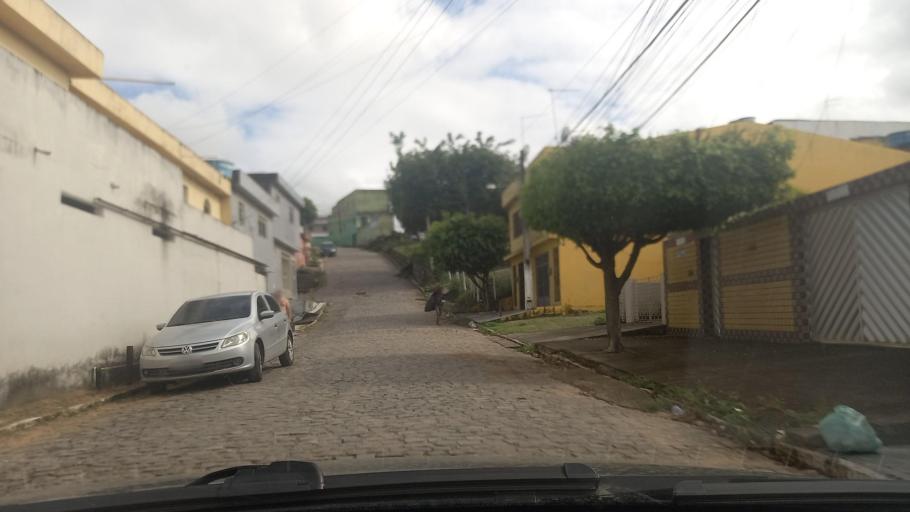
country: BR
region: Pernambuco
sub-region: Vitoria De Santo Antao
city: Vitoria de Santo Antao
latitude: -8.1101
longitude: -35.2965
